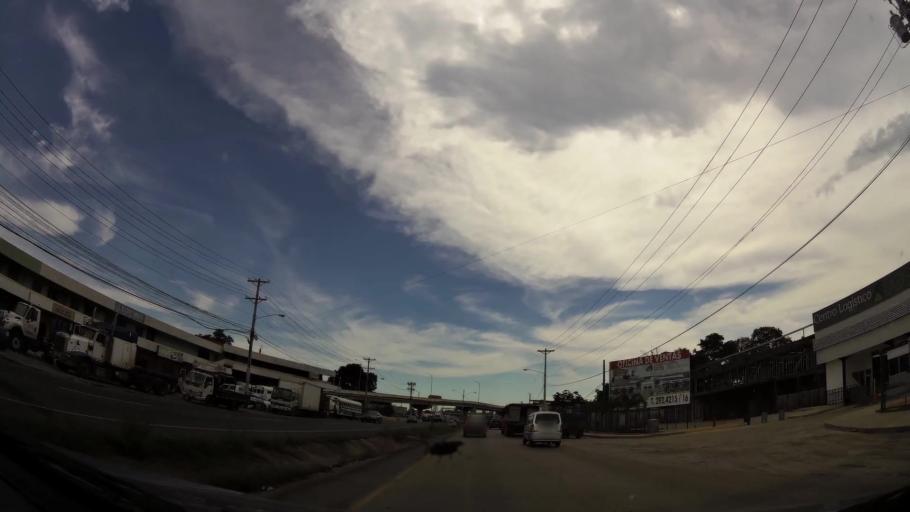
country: PA
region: Panama
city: Tocumen
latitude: 9.0824
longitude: -79.3990
